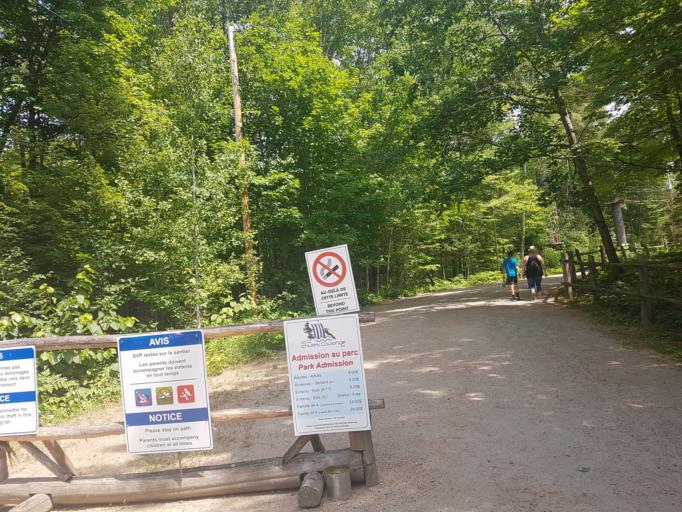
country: CA
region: Quebec
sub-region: Outaouais
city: Fort-Coulonge
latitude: 45.8760
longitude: -76.6882
